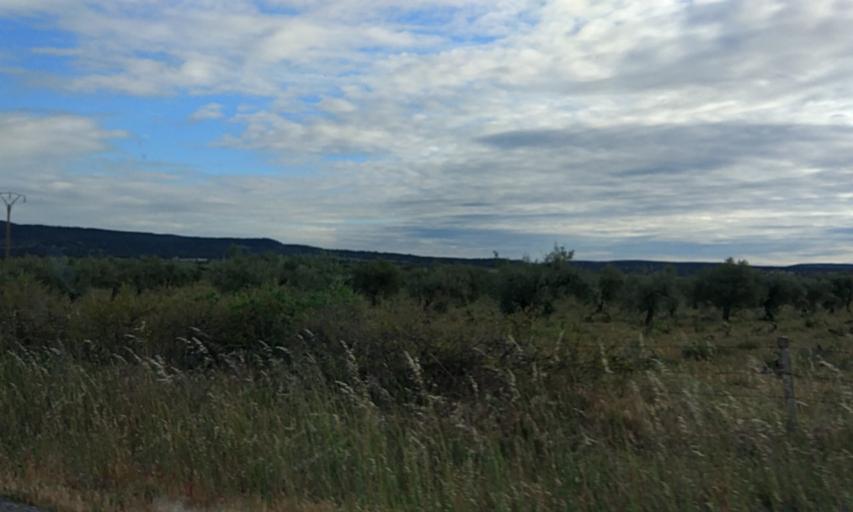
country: ES
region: Extremadura
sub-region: Provincia de Caceres
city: Torrejoncillo
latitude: 39.8736
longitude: -6.4445
